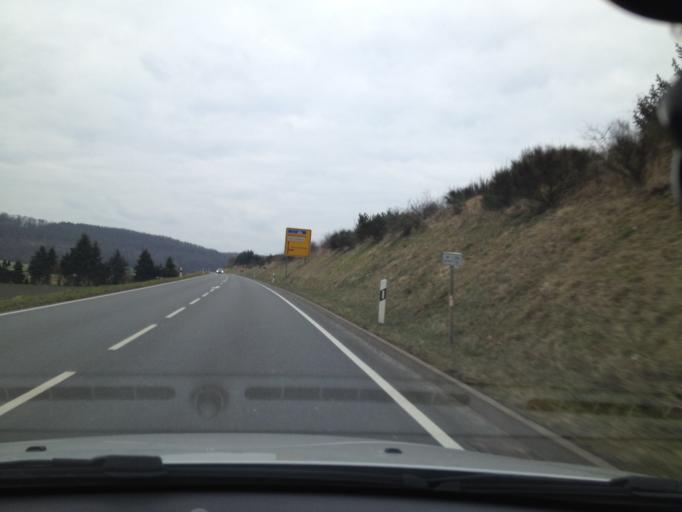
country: DE
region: Bavaria
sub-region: Regierungsbezirk Unterfranken
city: Kreuzwertheim
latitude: 49.7735
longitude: 9.5297
